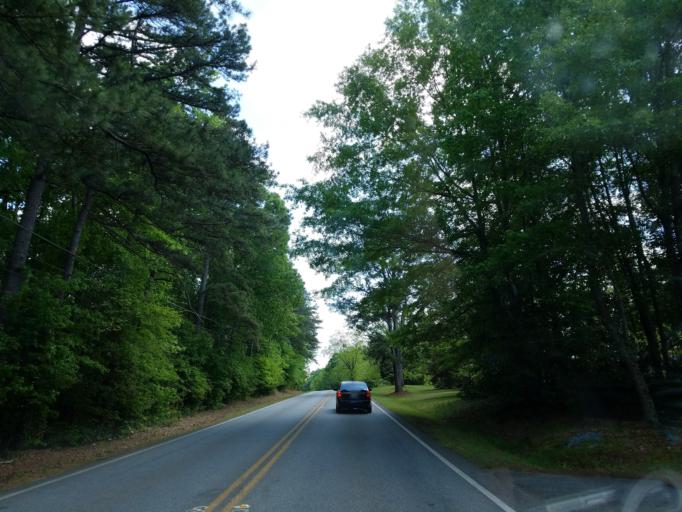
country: US
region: Georgia
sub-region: Monroe County
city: Forsyth
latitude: 33.0633
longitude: -83.9529
